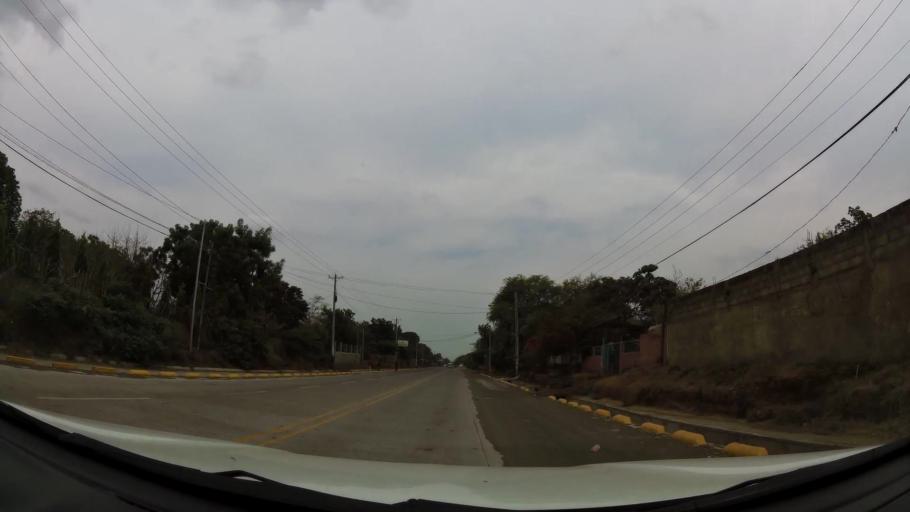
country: NI
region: Managua
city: Managua
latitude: 12.1212
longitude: -86.1701
